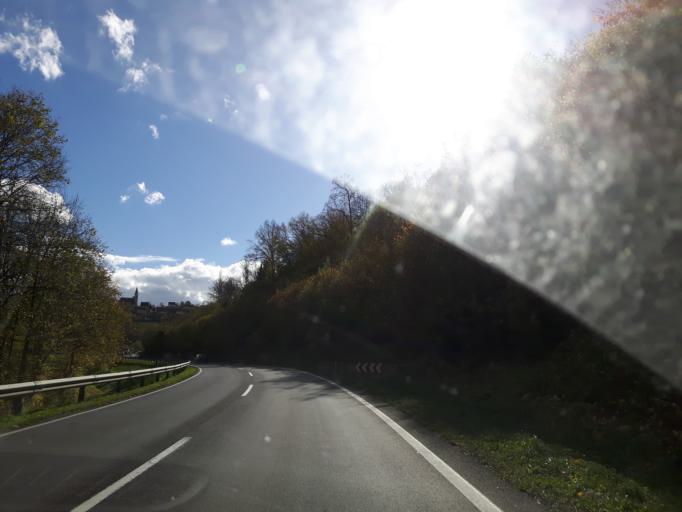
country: AT
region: Styria
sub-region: Politischer Bezirk Leibnitz
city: Seggauberg
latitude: 46.7835
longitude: 15.5169
